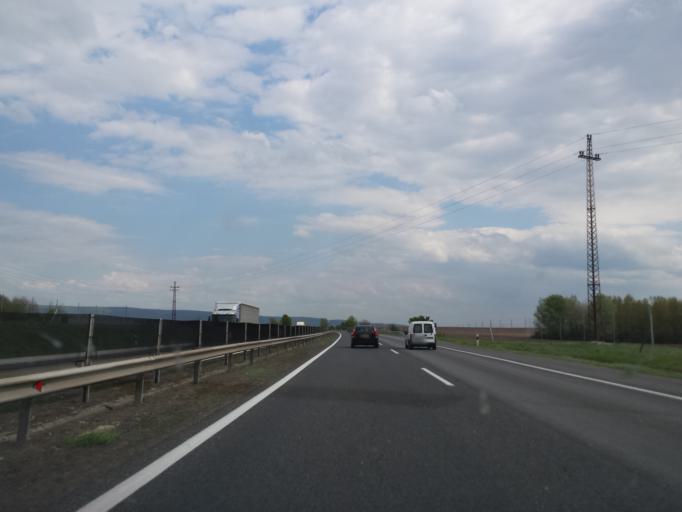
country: HU
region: Komarom-Esztergom
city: Kocs
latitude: 47.6271
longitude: 18.2665
